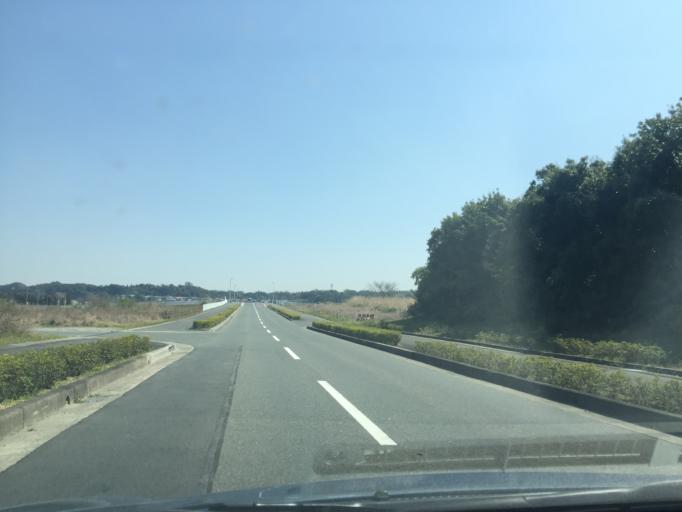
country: JP
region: Shizuoka
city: Hamamatsu
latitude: 34.7967
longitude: 137.6425
